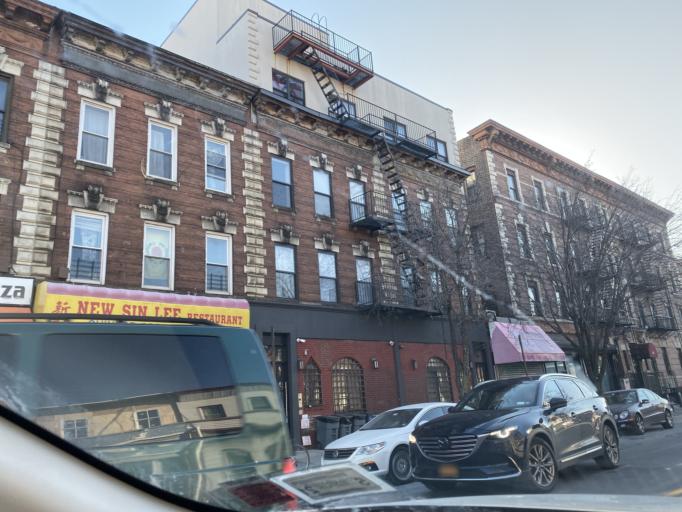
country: US
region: New York
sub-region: Kings County
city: Brooklyn
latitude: 40.6819
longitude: -73.9289
